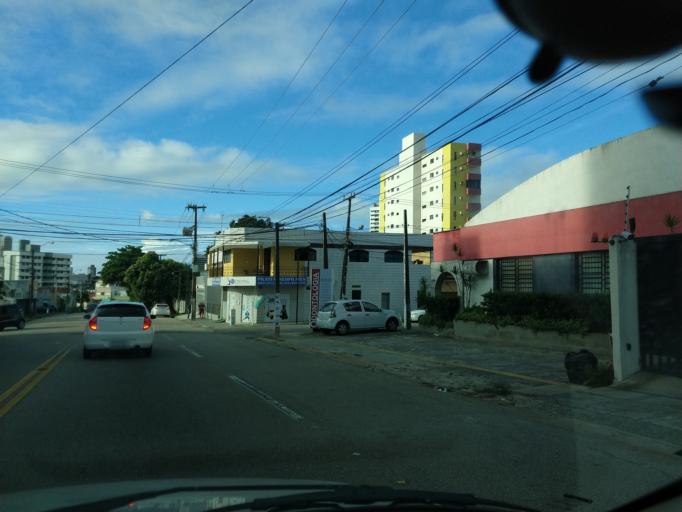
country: BR
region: Rio Grande do Norte
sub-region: Natal
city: Natal
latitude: -5.7960
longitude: -35.2095
